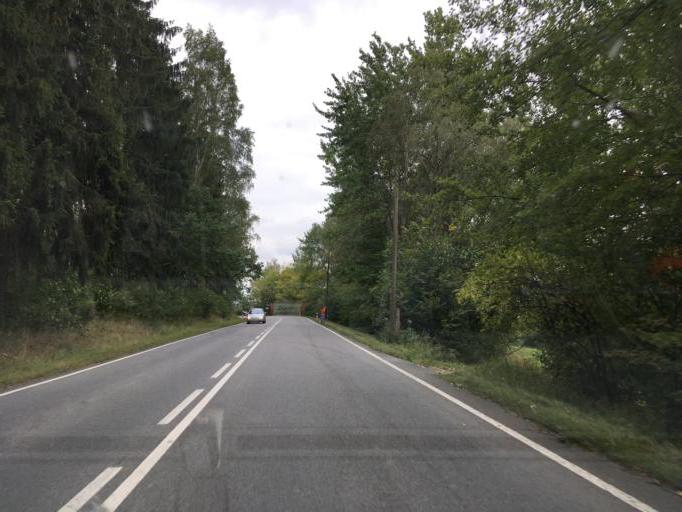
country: CZ
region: Vysocina
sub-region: Okres Pelhrimov
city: Pelhrimov
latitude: 49.4618
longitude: 15.1842
